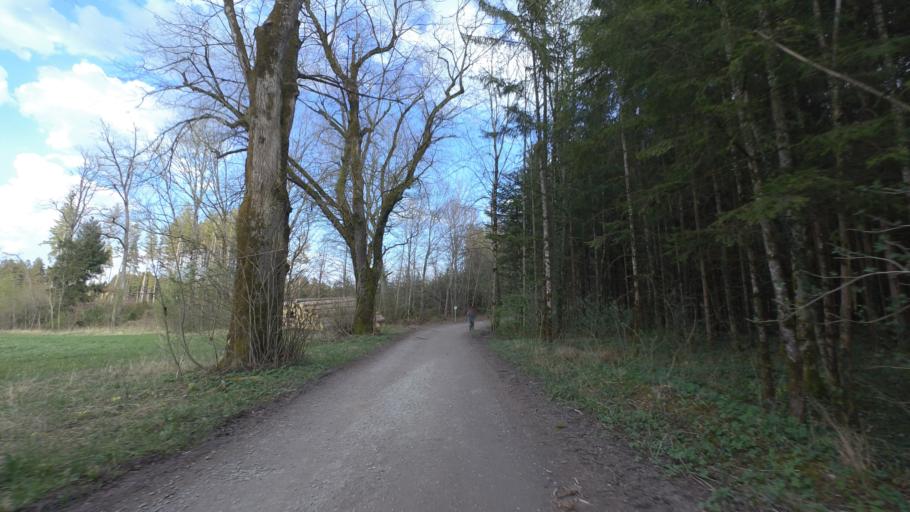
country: DE
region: Bavaria
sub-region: Upper Bavaria
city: Chieming
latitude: 47.9246
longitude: 12.5145
